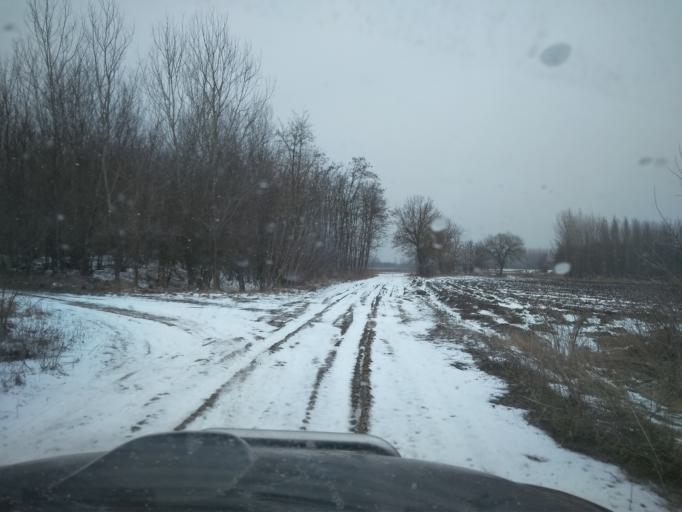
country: HU
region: Szabolcs-Szatmar-Bereg
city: Apagy
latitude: 47.9747
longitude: 21.9164
